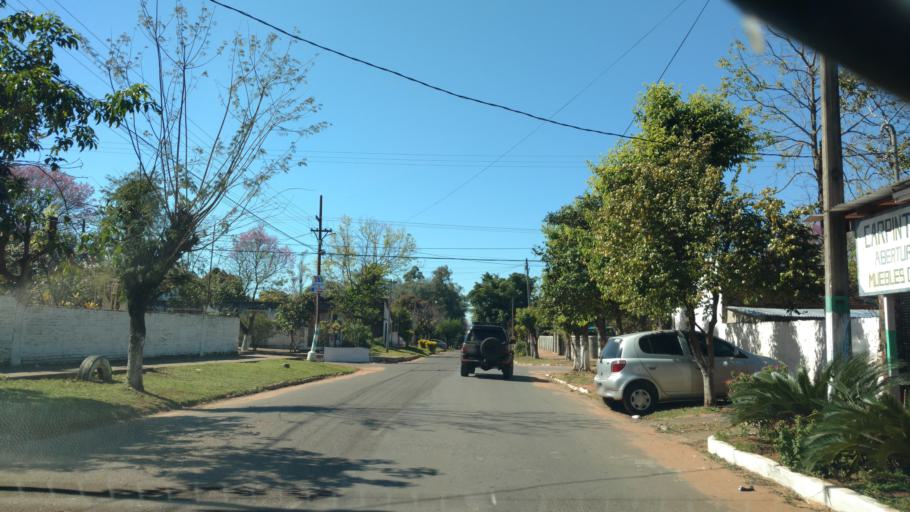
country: PY
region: Paraguari
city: Yaguaron
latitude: -25.5598
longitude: -57.2877
